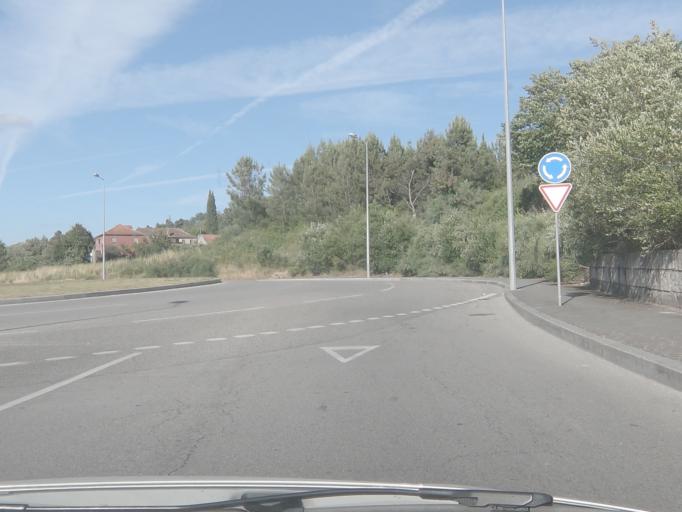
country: PT
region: Viseu
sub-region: Viseu
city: Rio de Loba
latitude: 40.6659
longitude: -7.8934
